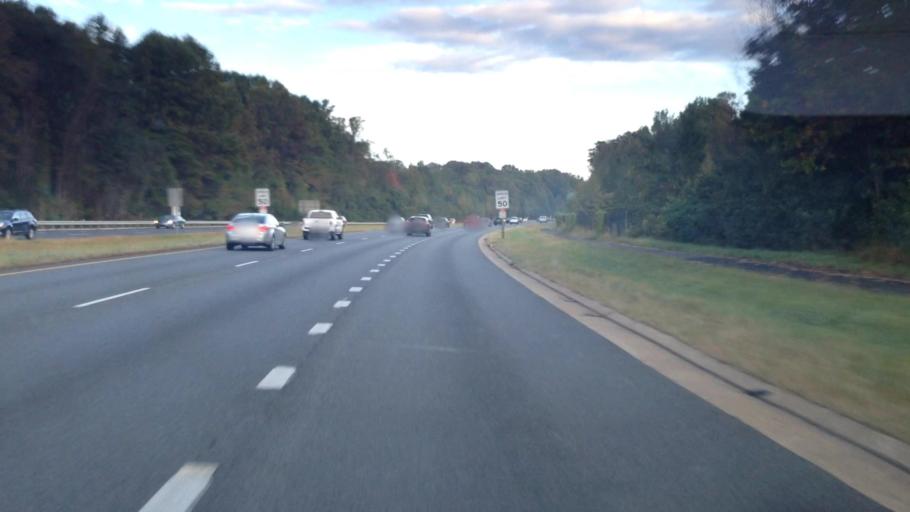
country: US
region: Virginia
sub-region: Fairfax County
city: Greenbriar
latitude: 38.8343
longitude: -77.3718
